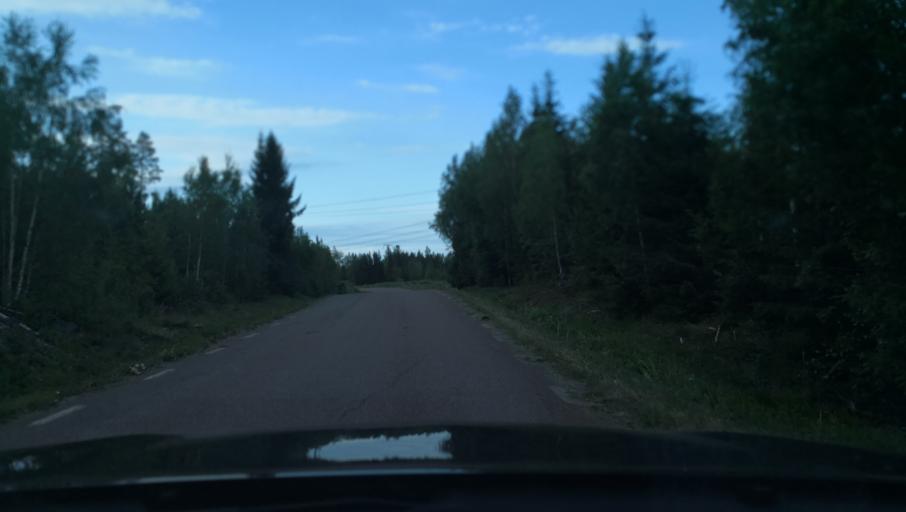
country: SE
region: Dalarna
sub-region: Ludvika Kommun
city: Ludvika
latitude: 60.1087
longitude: 15.2660
